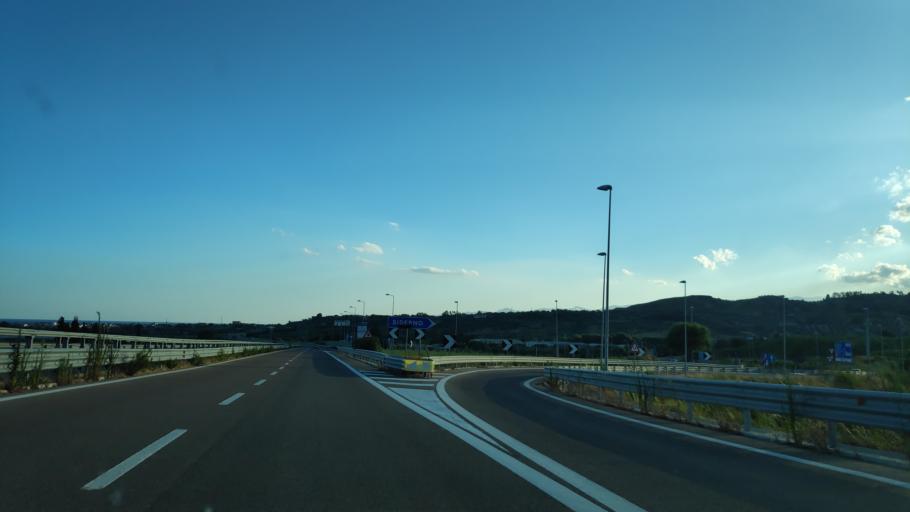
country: IT
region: Calabria
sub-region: Provincia di Reggio Calabria
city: Siderno
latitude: 38.2697
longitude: 16.2678
